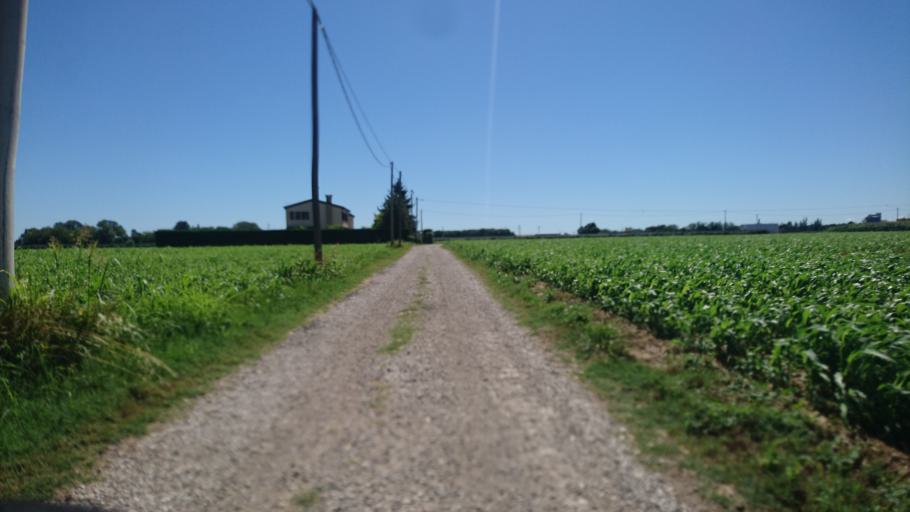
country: IT
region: Veneto
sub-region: Provincia di Padova
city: Pontelongo
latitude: 45.2570
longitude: 12.0182
